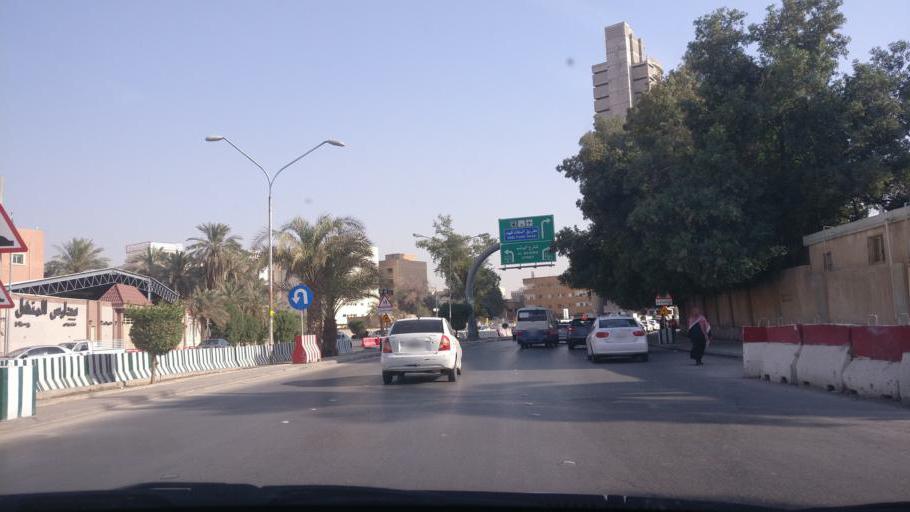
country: SA
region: Ar Riyad
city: Riyadh
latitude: 24.6550
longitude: 46.7098
